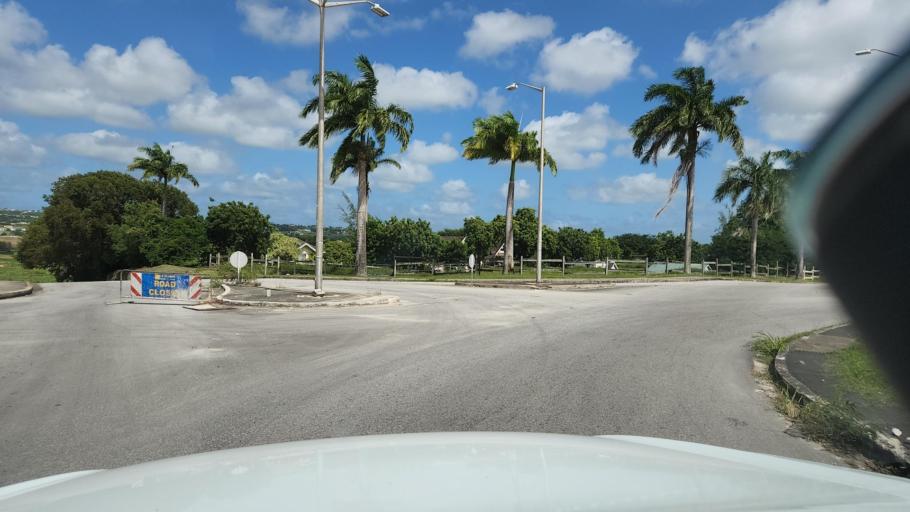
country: BB
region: Christ Church
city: Oistins
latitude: 13.1080
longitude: -59.5421
